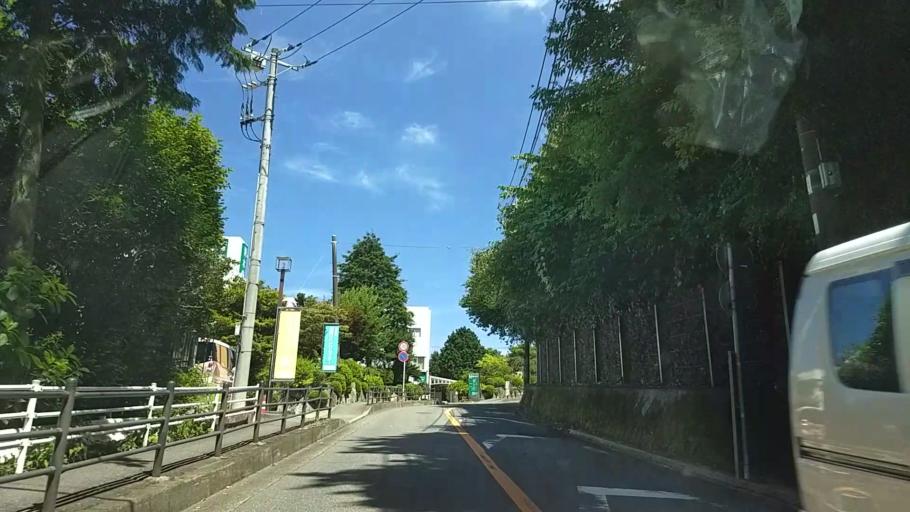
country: JP
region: Kanagawa
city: Zushi
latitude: 35.2924
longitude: 139.5901
